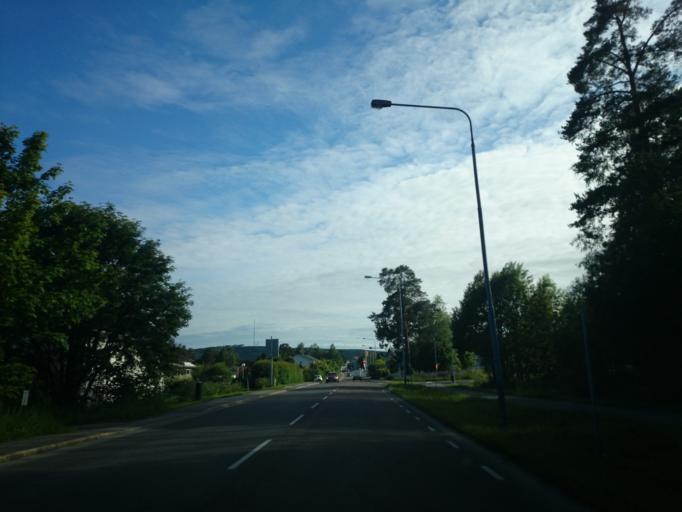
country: SE
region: Vaesternorrland
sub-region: Sundsvalls Kommun
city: Sundsvall
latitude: 62.4040
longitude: 17.3302
